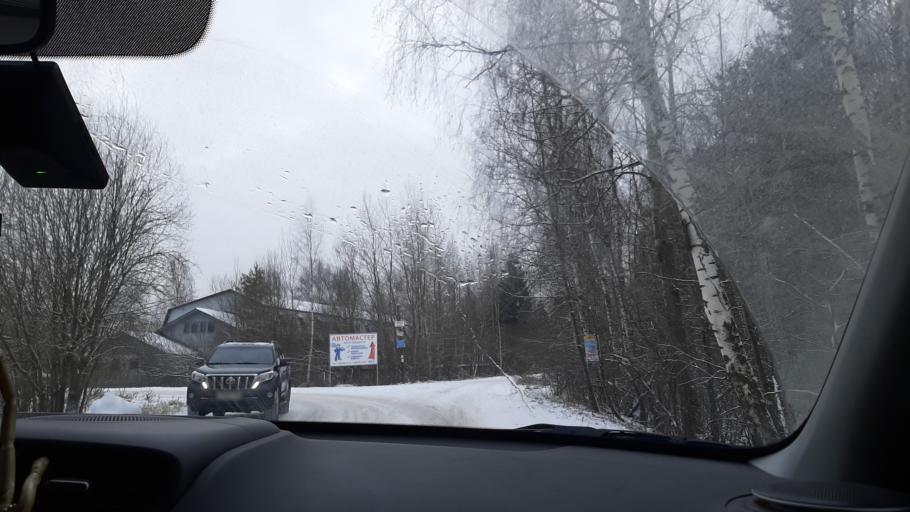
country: RU
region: Ivanovo
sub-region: Gorod Ivanovo
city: Ivanovo
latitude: 56.9290
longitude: 40.9769
